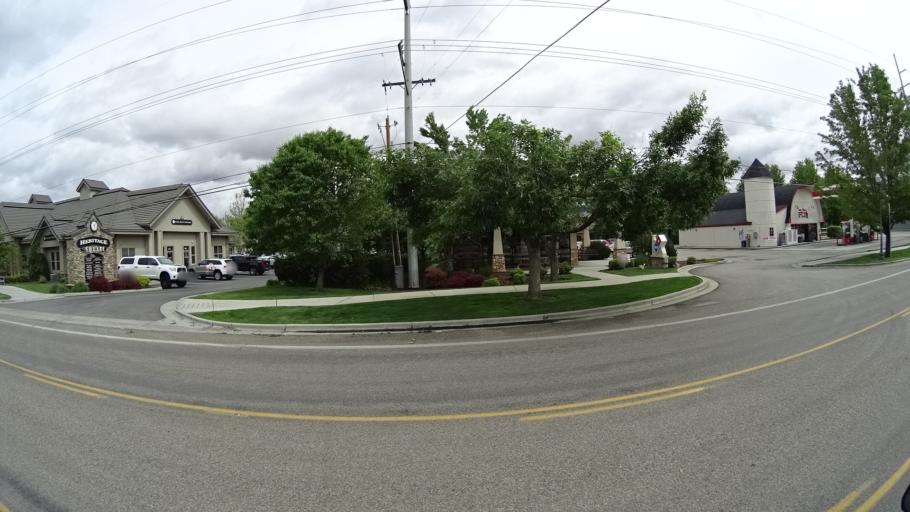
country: US
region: Idaho
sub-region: Ada County
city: Eagle
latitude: 43.6951
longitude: -116.3481
